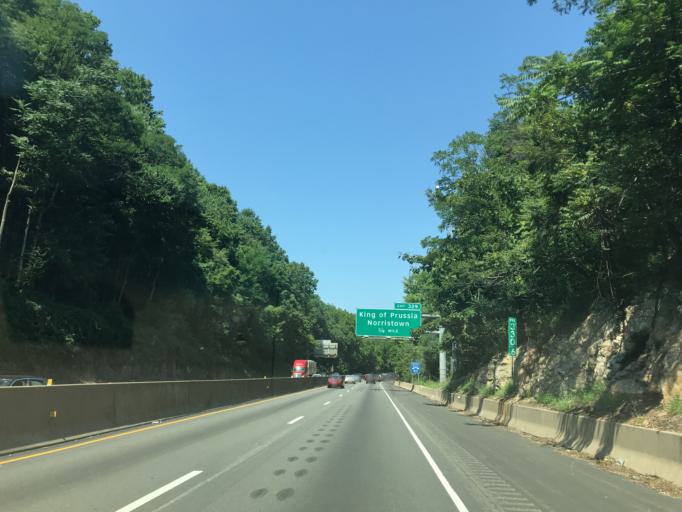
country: US
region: Pennsylvania
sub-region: Montgomery County
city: West Conshohocken
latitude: 40.0674
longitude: -75.3367
